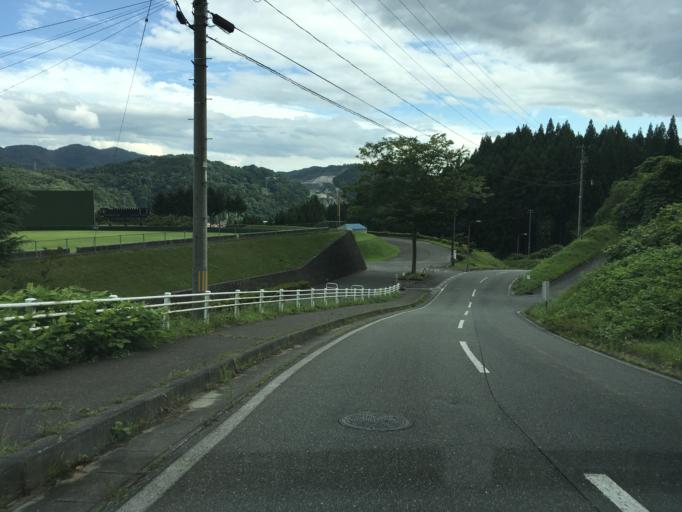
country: JP
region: Iwate
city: Ichinoseki
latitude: 38.9986
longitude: 141.2504
